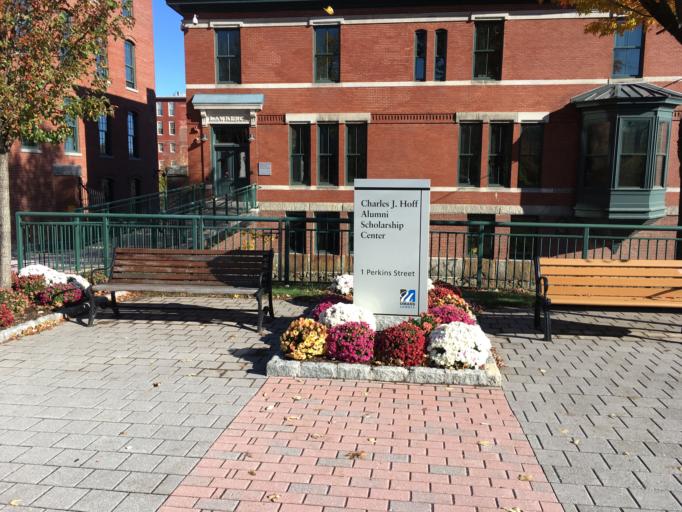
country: US
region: Massachusetts
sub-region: Middlesex County
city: Lowell
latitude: 42.6512
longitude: -71.3144
